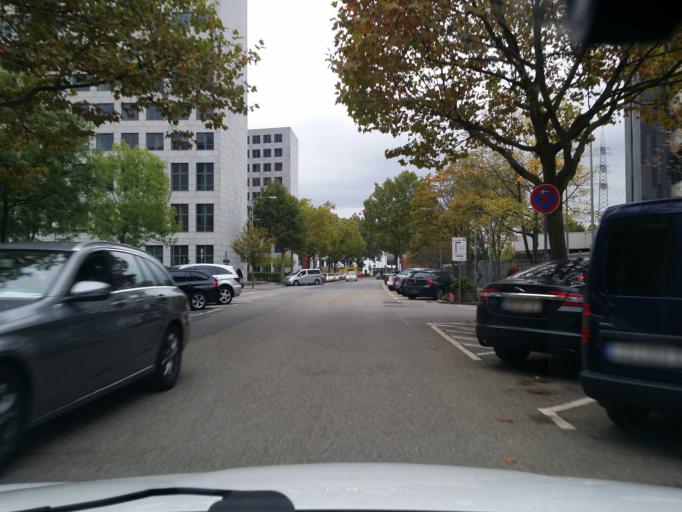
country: DE
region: Hesse
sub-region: Regierungsbezirk Darmstadt
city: Eschborn
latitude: 50.1337
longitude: 8.5743
